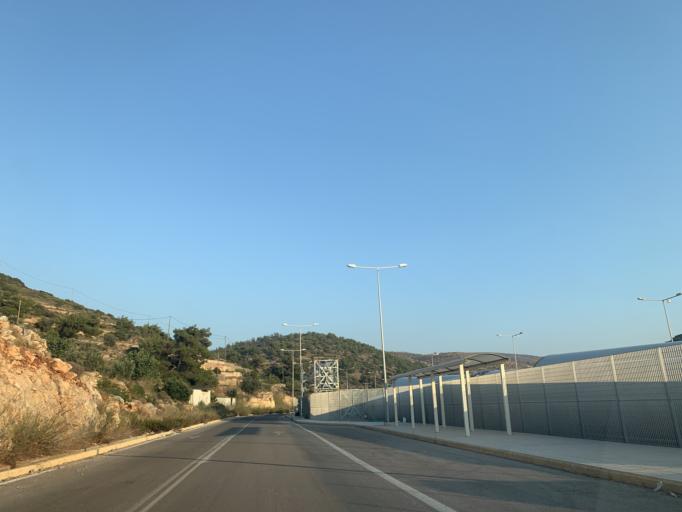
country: GR
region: North Aegean
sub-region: Chios
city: Thymiana
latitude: 38.2913
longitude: 25.9297
